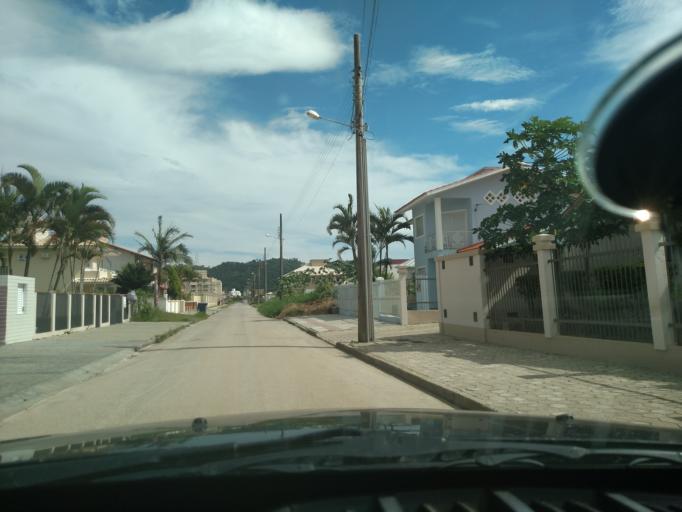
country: BR
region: Santa Catarina
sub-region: Tijucas
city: Tijucas
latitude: -27.3310
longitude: -48.5358
